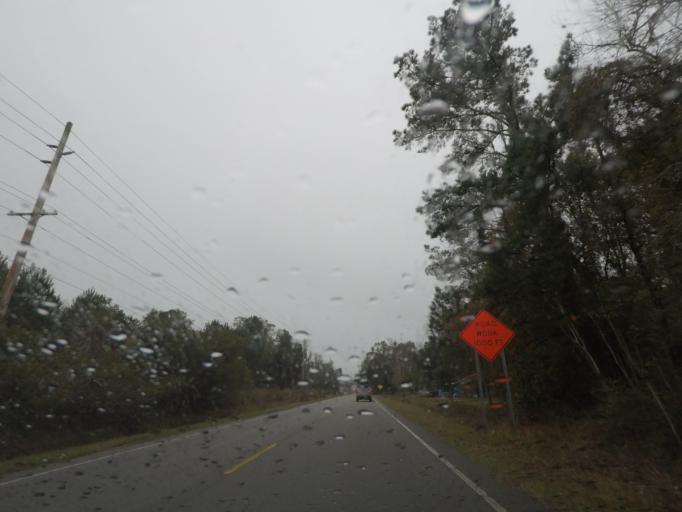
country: US
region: South Carolina
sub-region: Charleston County
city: Seabrook Island
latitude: 32.5650
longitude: -80.2815
